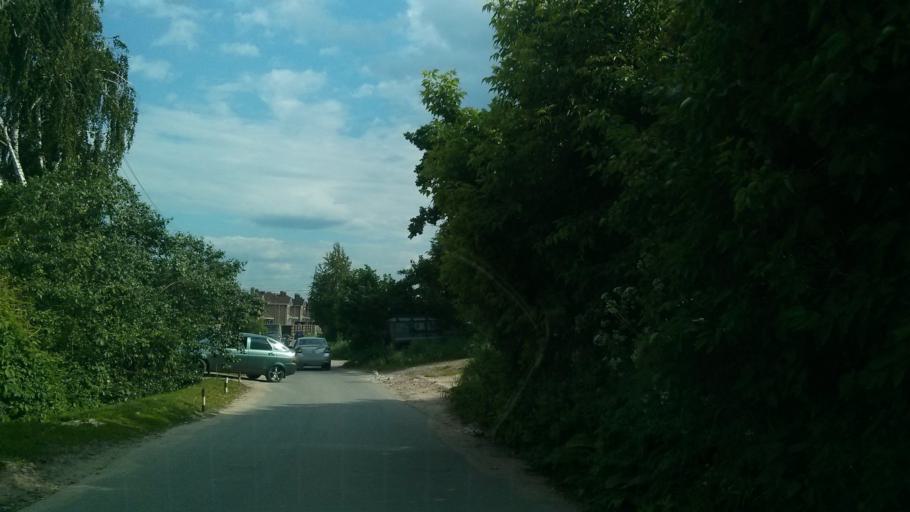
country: RU
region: Nizjnij Novgorod
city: Afonino
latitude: 56.2840
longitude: 44.1009
